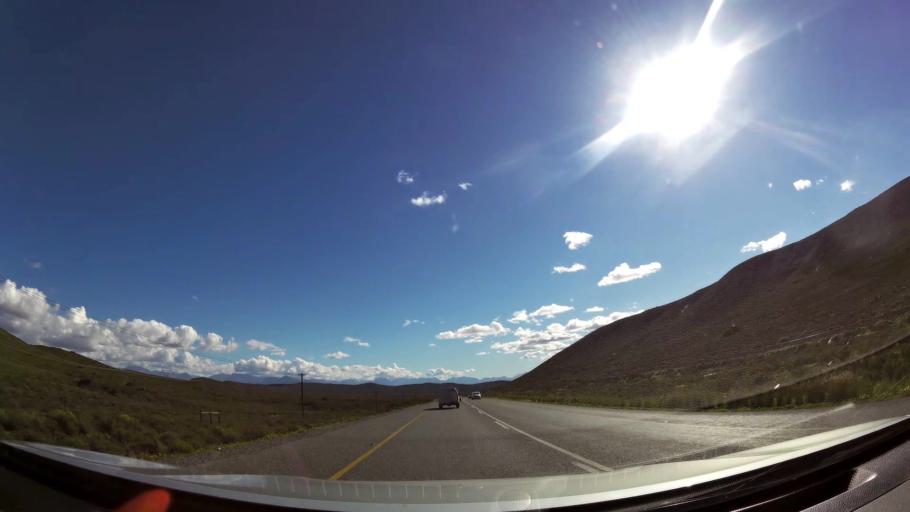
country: ZA
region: Western Cape
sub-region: Cape Winelands District Municipality
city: Worcester
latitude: -33.7345
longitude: 19.6542
